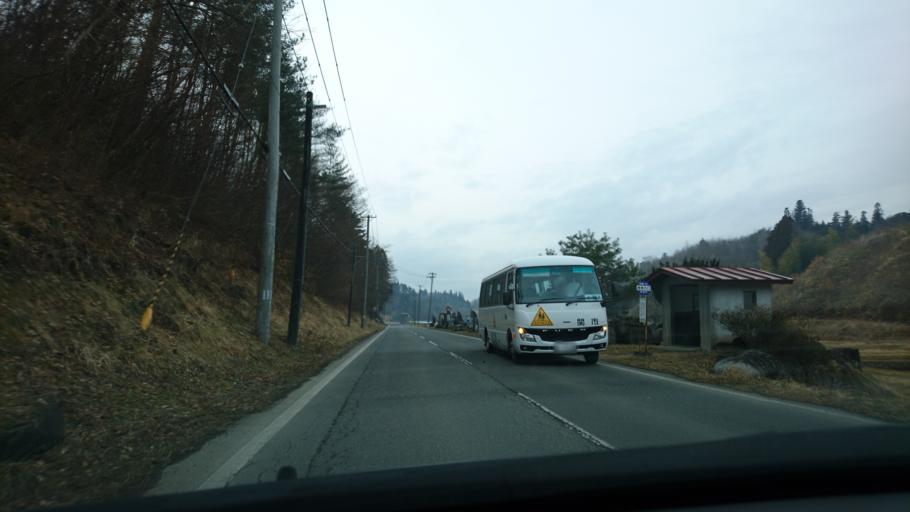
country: JP
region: Iwate
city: Ichinoseki
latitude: 38.9068
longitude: 141.3762
